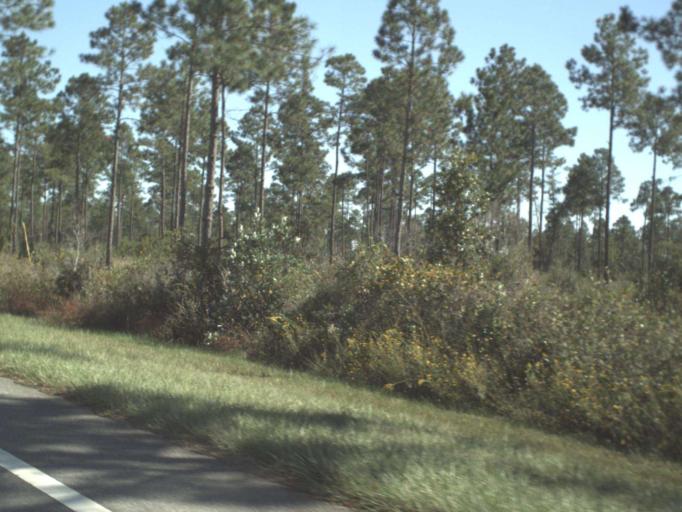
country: US
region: Florida
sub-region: Bay County
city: Lynn Haven
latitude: 30.3282
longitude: -85.7389
